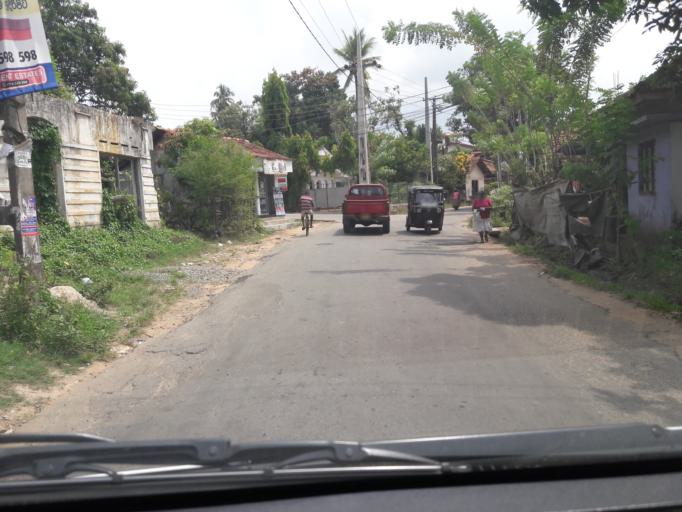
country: LK
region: Southern
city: Hikkaduwa
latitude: 6.0936
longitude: 80.1439
